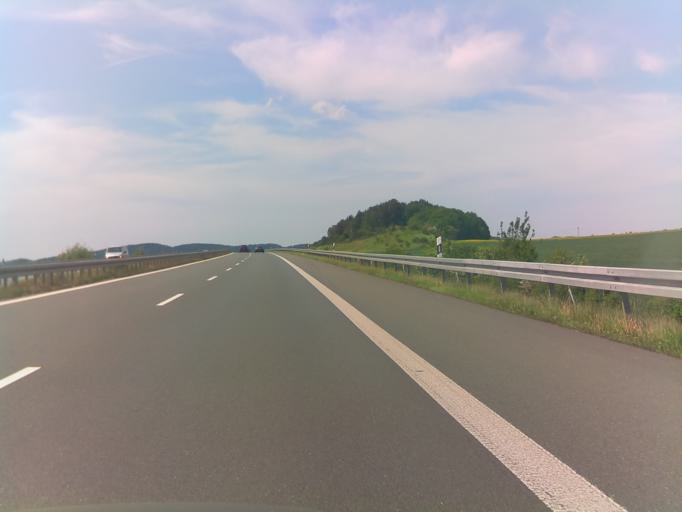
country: DE
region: Saxony-Anhalt
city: Westerhausen
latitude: 51.8151
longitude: 11.0893
